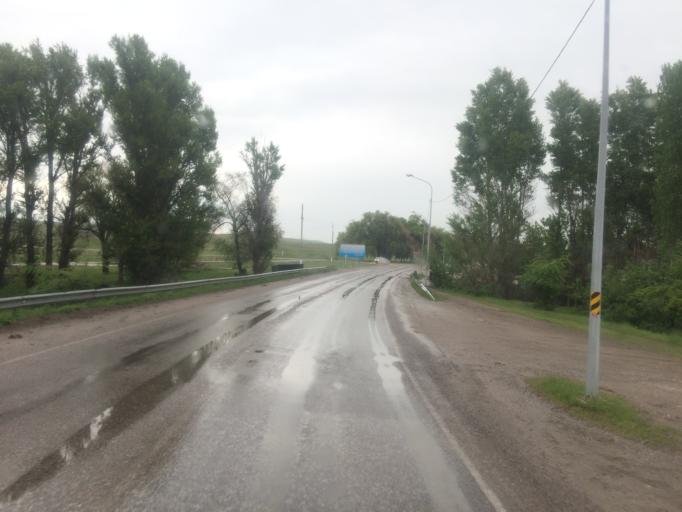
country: KZ
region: Zhambyl
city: Georgiyevka
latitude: 43.2358
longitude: 74.7592
